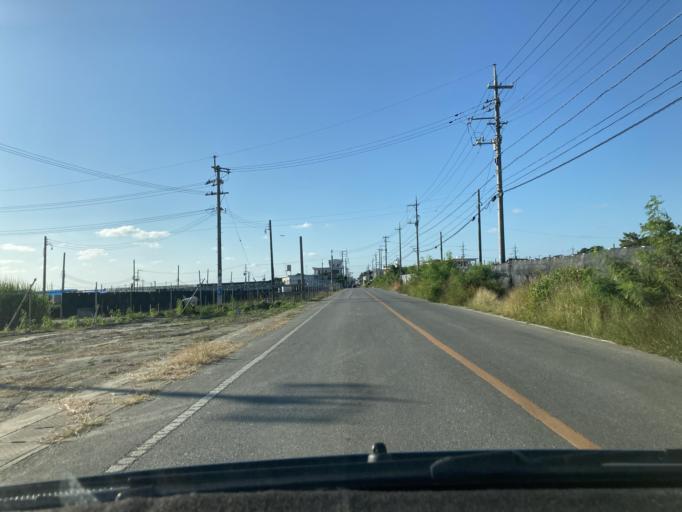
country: JP
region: Okinawa
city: Itoman
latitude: 26.1023
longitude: 127.6708
